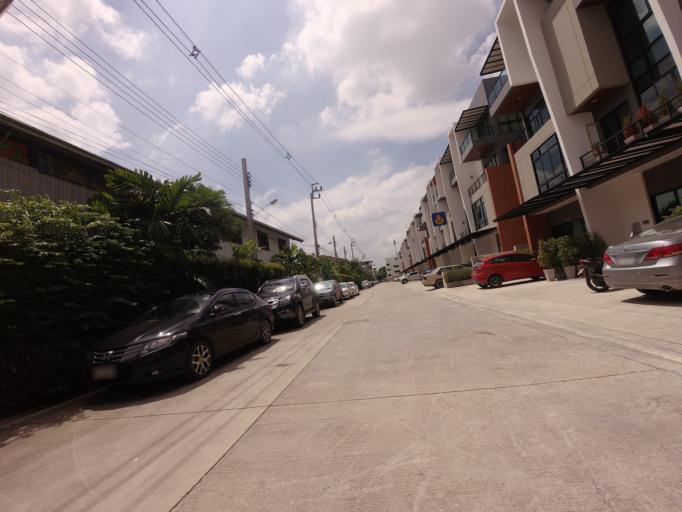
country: TH
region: Bangkok
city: Bueng Kum
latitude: 13.7937
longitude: 100.6537
